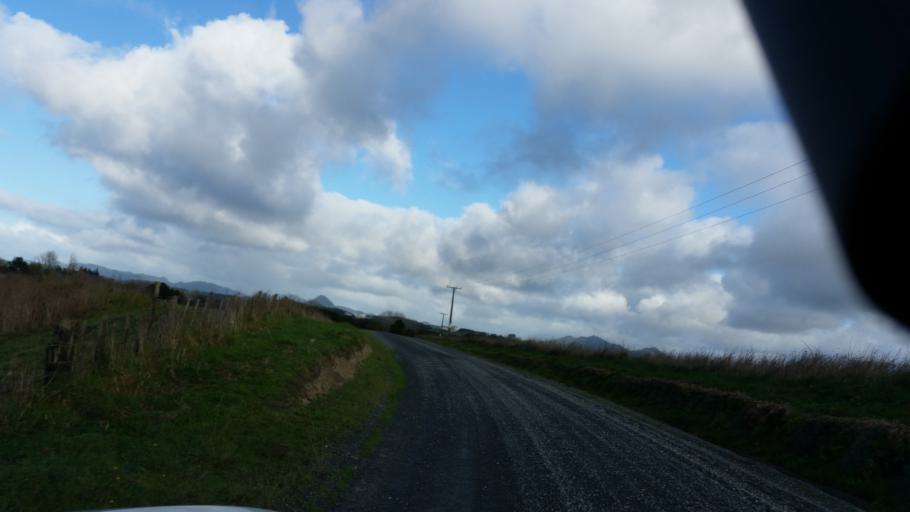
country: NZ
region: Northland
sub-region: Whangarei
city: Maungatapere
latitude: -35.7183
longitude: 174.0733
